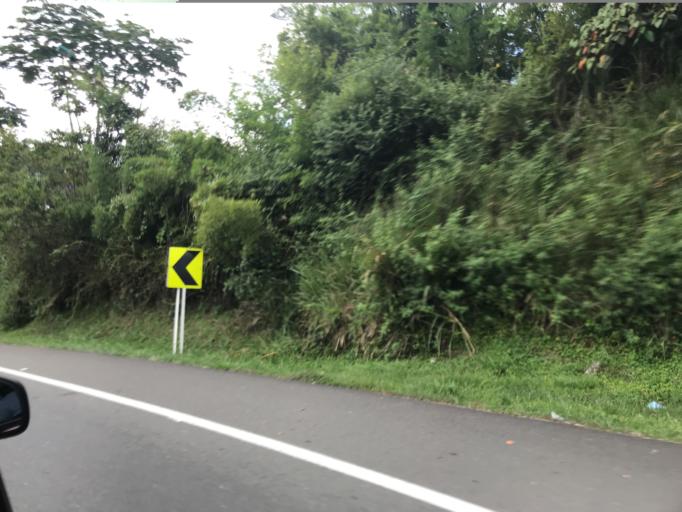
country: CO
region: Quindio
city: Armenia
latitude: 4.4964
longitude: -75.6842
